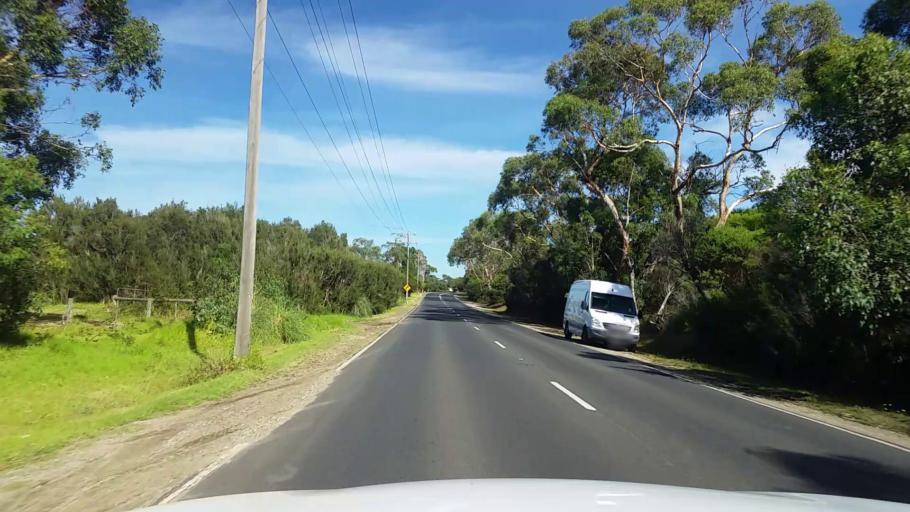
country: AU
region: Victoria
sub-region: Mornington Peninsula
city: Baxter
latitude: -38.1961
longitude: 145.1426
